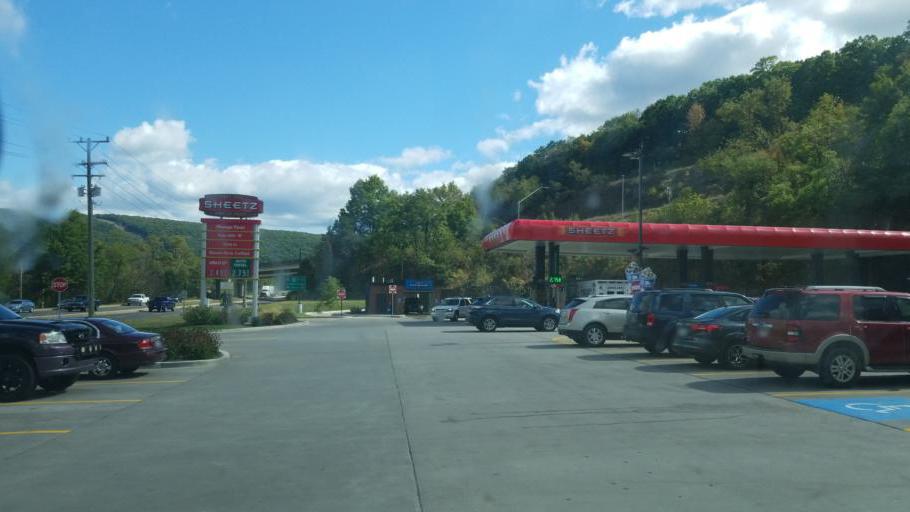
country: US
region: Maryland
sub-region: Allegany County
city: La Vale
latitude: 39.6361
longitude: -78.8452
